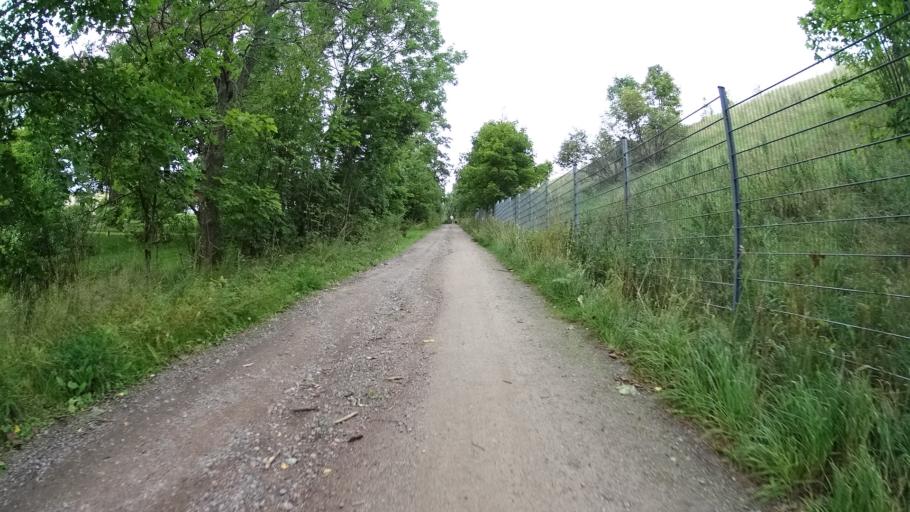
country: FI
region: Uusimaa
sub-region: Helsinki
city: Teekkarikylae
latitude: 60.2788
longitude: 24.8888
